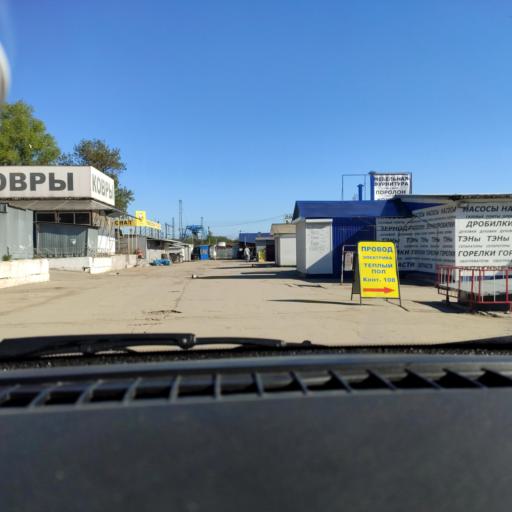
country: RU
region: Samara
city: Samara
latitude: 53.2087
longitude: 50.2533
